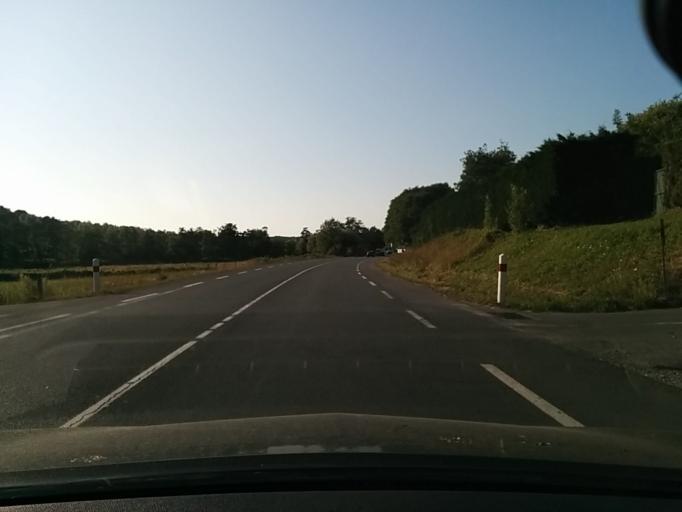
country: FR
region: Aquitaine
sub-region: Departement des Pyrenees-Atlantiques
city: Ciboure
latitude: 43.3748
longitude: -1.6853
